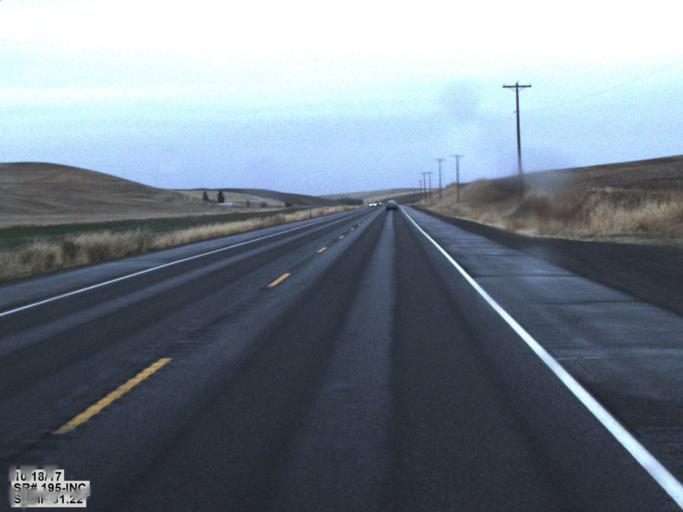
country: US
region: Washington
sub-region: Whitman County
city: Colfax
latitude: 46.7998
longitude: -117.3155
